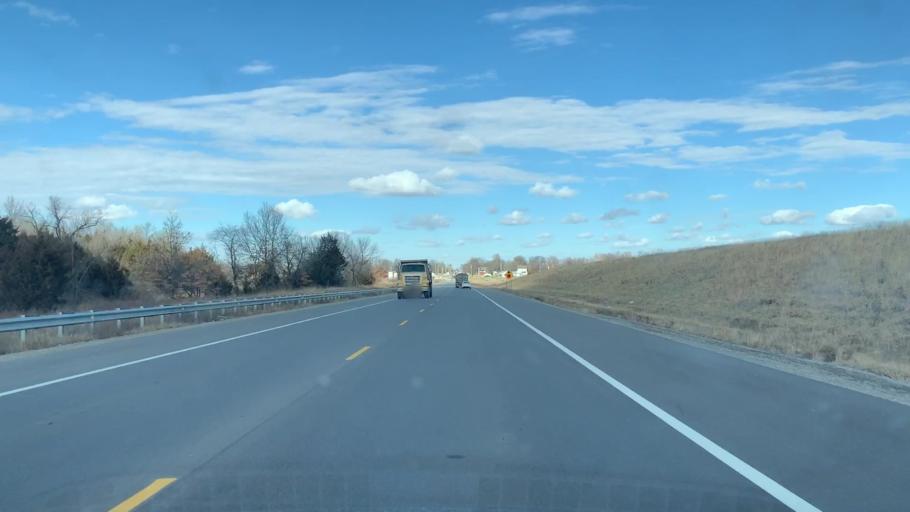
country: US
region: Kansas
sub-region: Crawford County
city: Pittsburg
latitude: 37.3341
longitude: -94.8321
